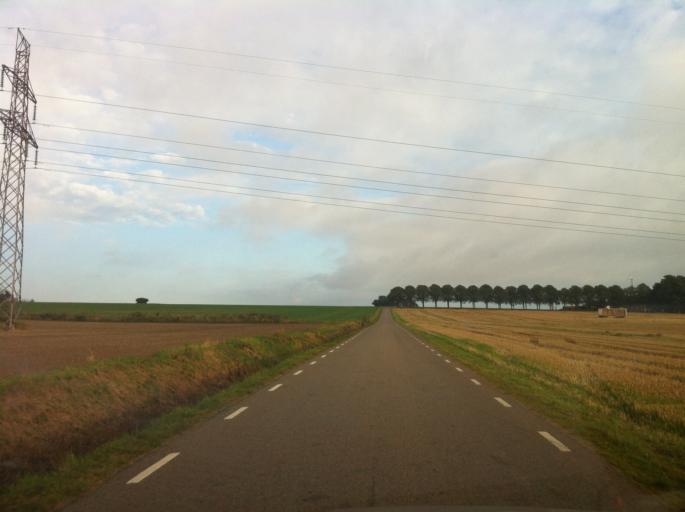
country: SE
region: Skane
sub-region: Helsingborg
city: Glumslov
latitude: 55.9648
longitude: 12.8925
